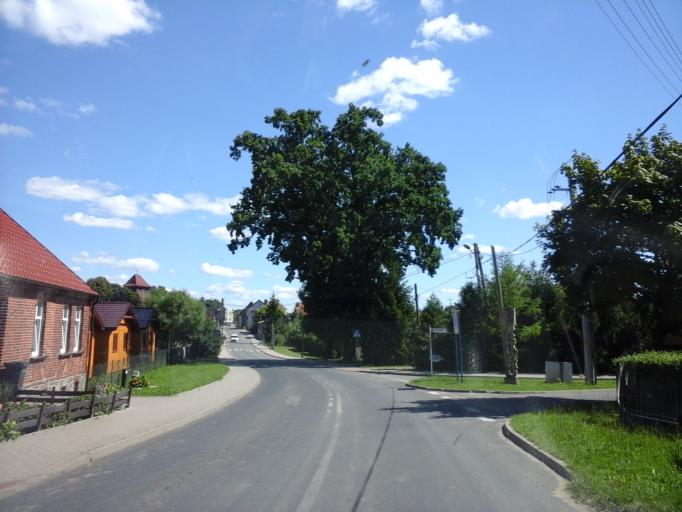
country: PL
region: West Pomeranian Voivodeship
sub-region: Powiat choszczenski
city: Drawno
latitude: 53.2223
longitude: 15.7547
